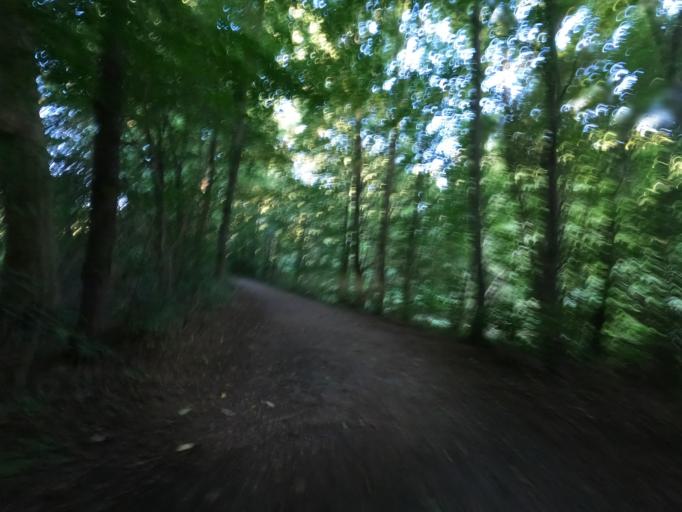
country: DE
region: North Rhine-Westphalia
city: Julich
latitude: 50.9452
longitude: 6.3146
